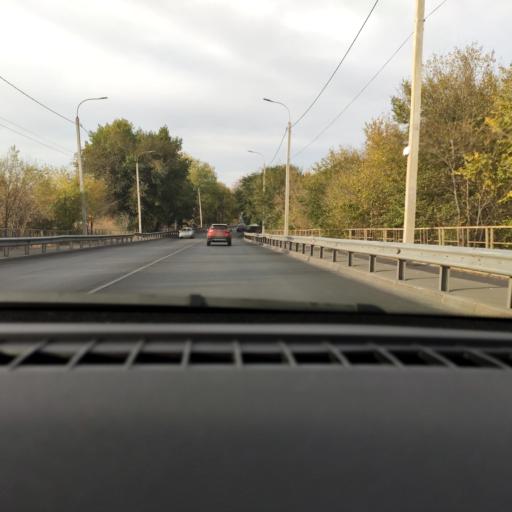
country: RU
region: Voronezj
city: Voronezh
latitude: 51.7276
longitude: 39.2603
